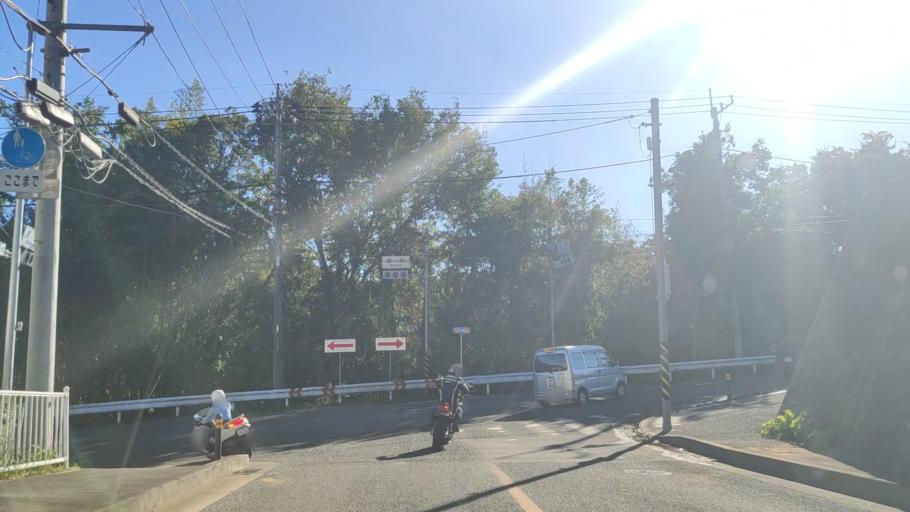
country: JP
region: Tokyo
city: Hachioji
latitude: 35.5846
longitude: 139.2957
